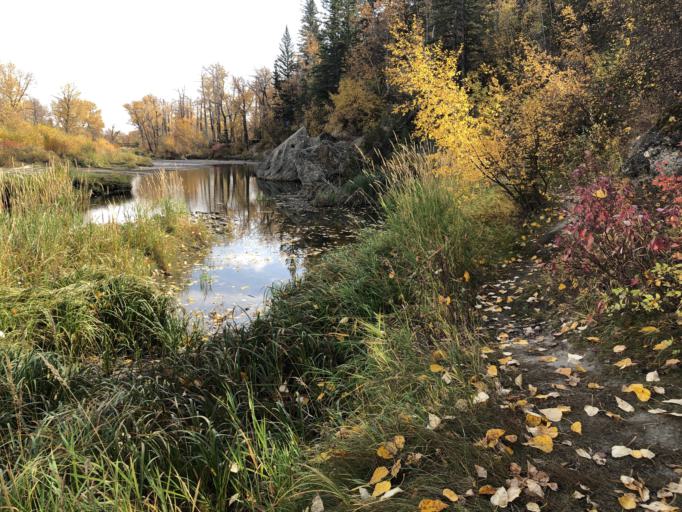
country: CA
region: Alberta
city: Calgary
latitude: 50.9068
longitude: -114.0252
